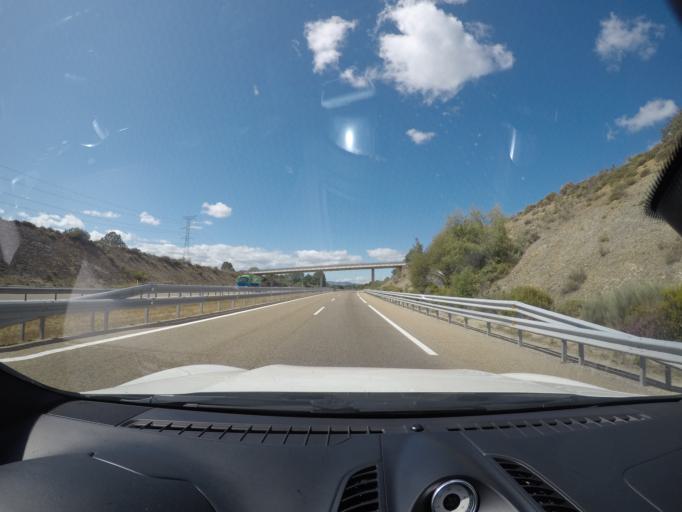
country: ES
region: Castille and Leon
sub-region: Provincia de Zamora
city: Palacios de Sanabria
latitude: 42.0488
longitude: -6.5300
